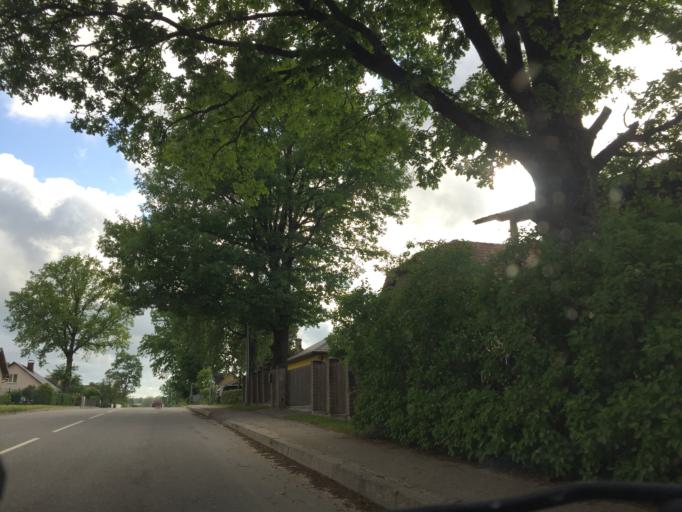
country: LV
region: Valmieras Rajons
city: Valmiera
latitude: 57.5445
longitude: 25.4115
